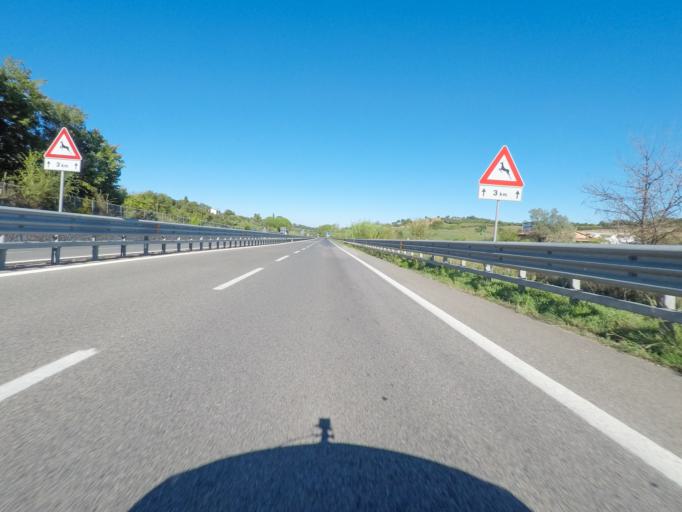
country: IT
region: Tuscany
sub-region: Provincia di Grosseto
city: Campagnatico
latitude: 42.8784
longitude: 11.2145
